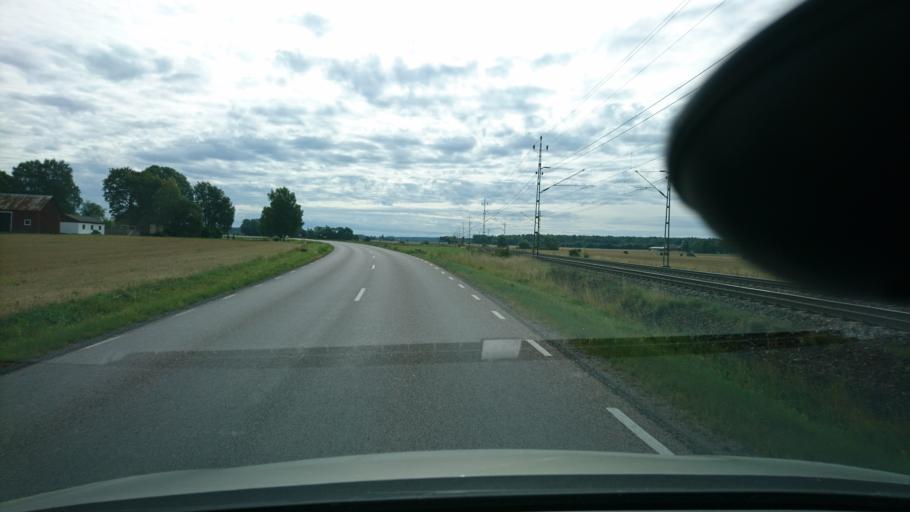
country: SE
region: Uppsala
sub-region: Uppsala Kommun
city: Saevja
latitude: 59.8328
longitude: 17.6958
